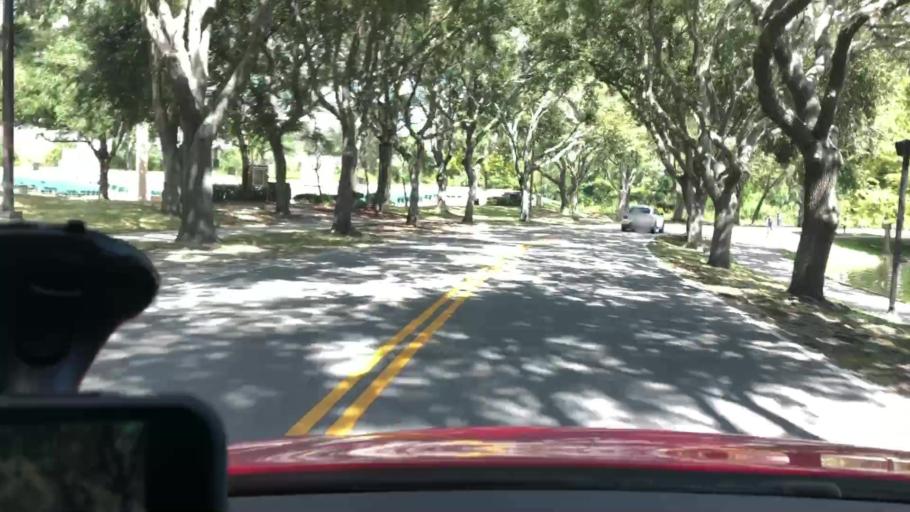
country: US
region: Florida
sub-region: Volusia County
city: Port Orange
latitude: 29.1269
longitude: -81.0221
